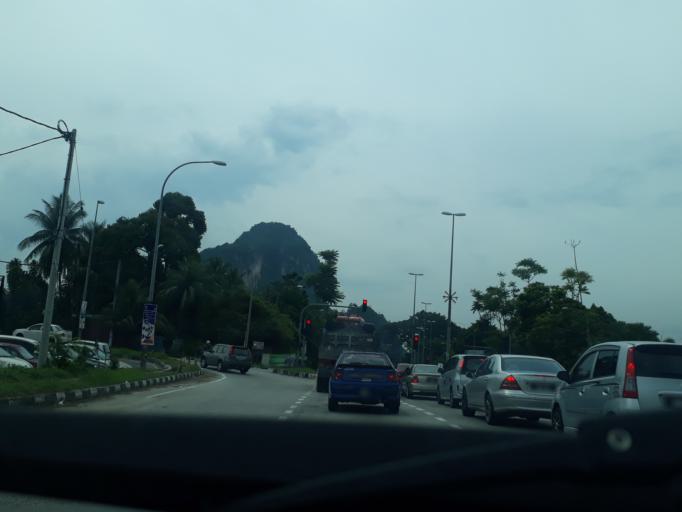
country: MY
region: Perak
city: Ipoh
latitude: 4.6367
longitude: 101.1546
